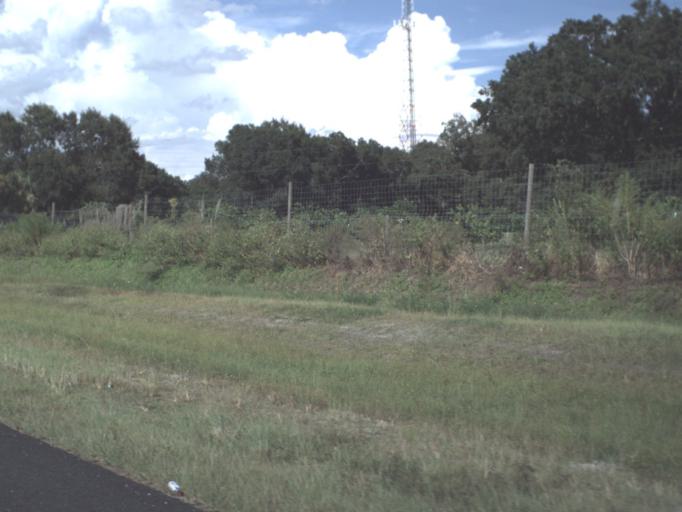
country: US
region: Florida
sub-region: Hardee County
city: Zolfo Springs
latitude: 27.4106
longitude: -81.7952
